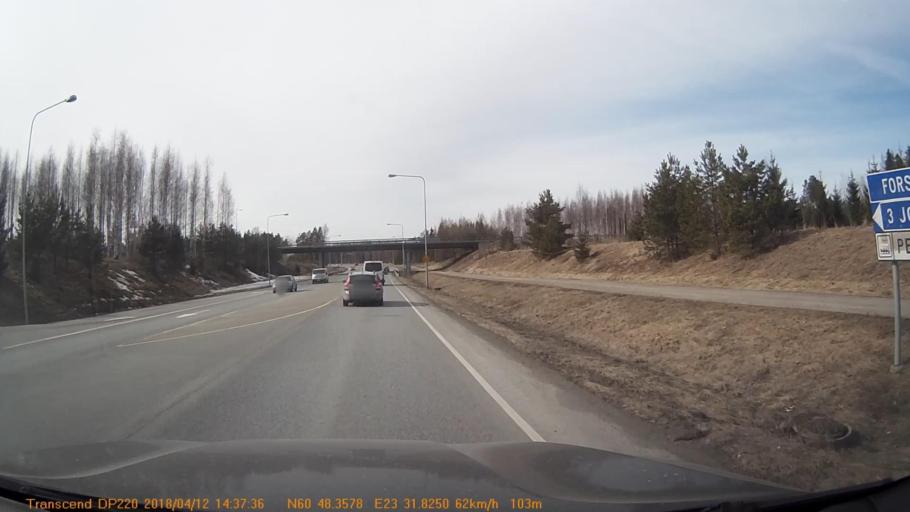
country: FI
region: Haeme
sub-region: Forssa
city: Jokioinen
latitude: 60.8066
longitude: 23.5284
